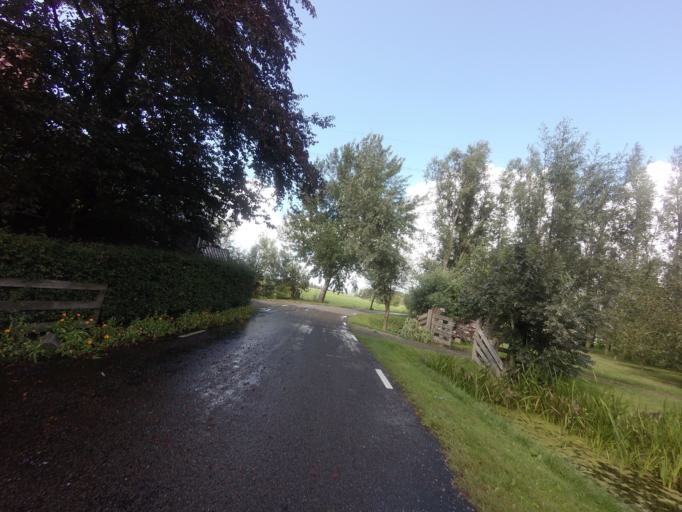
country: NL
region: Friesland
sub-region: Gemeente Leeuwarden
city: Wirdum
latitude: 53.1467
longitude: 5.7906
